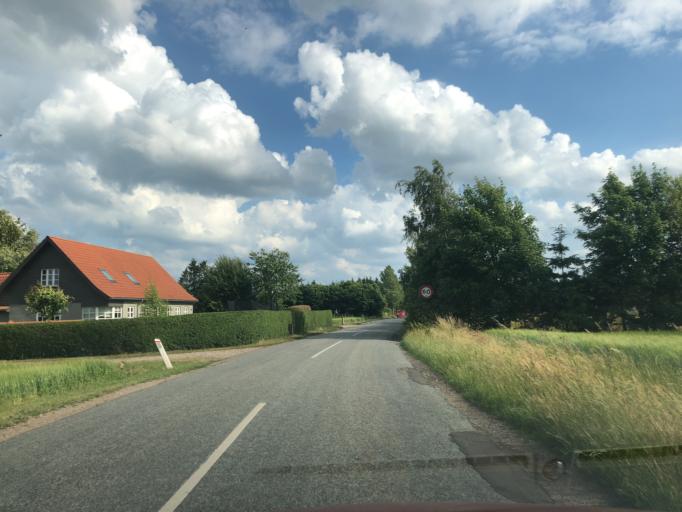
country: DK
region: Zealand
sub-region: Stevns Kommune
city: Harlev
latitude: 55.2867
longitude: 12.2197
